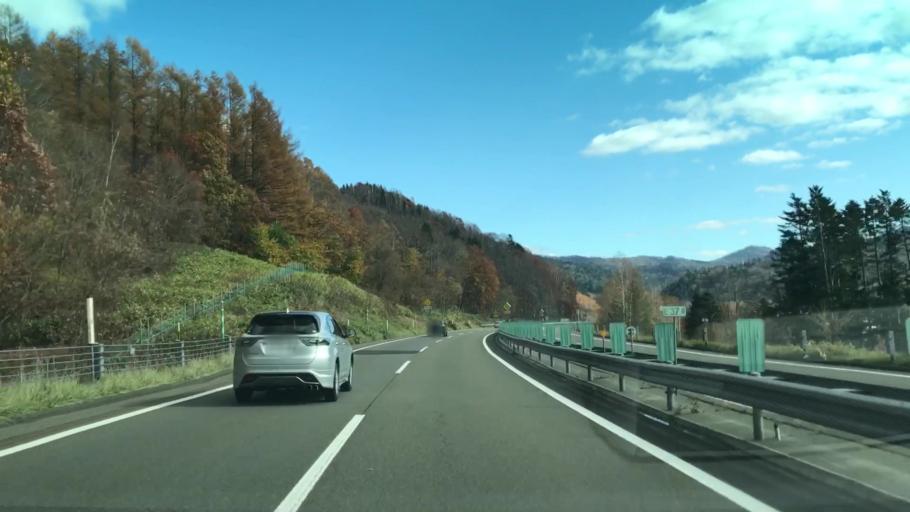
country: JP
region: Hokkaido
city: Chitose
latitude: 42.9078
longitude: 141.9955
